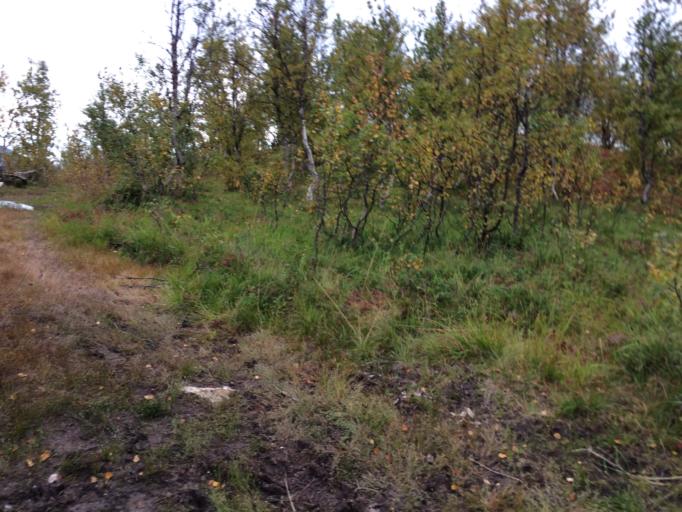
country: NO
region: Troms
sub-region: Sorreisa
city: Sorreisa
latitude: 69.5342
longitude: 18.3101
